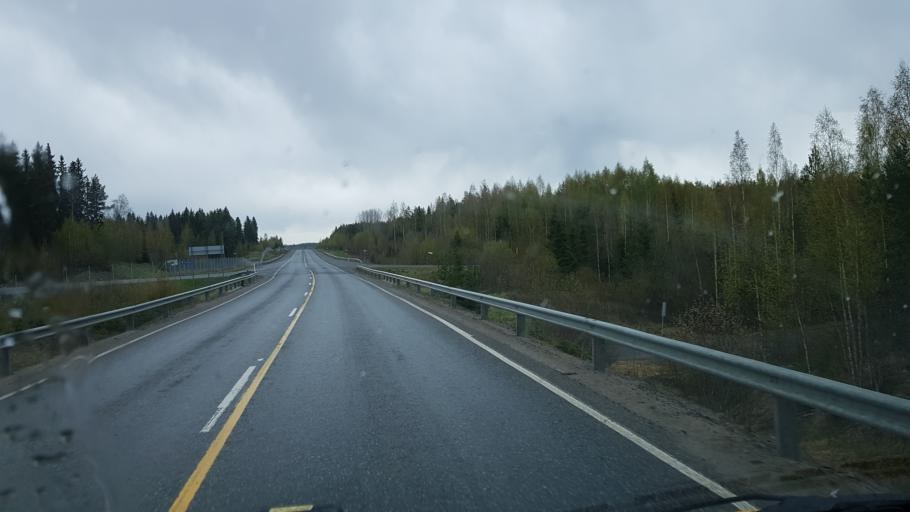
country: FI
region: Pirkanmaa
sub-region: Tampere
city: Pirkkala
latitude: 61.4086
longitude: 23.6338
